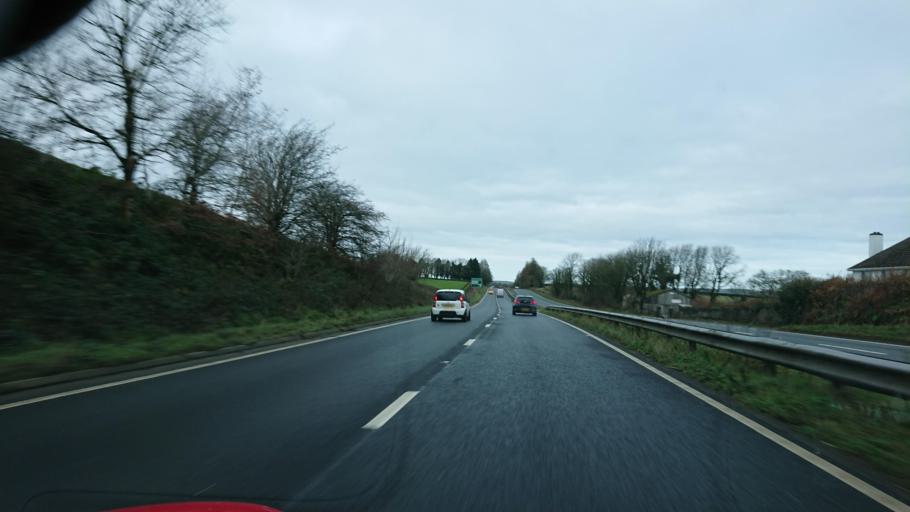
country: GB
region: England
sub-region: Cornwall
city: Liskeard
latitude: 50.4395
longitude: -4.4422
